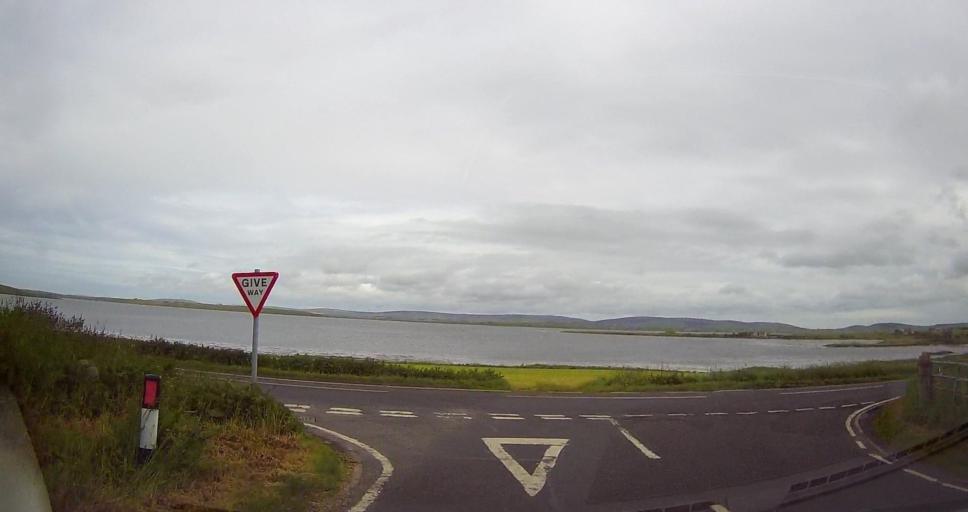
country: GB
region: Scotland
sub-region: Orkney Islands
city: Stromness
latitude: 58.9824
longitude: -3.2599
